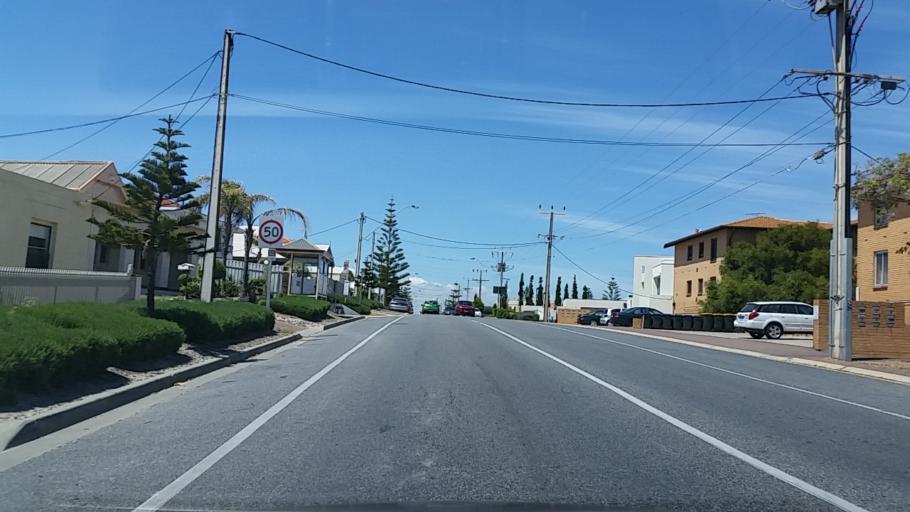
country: AU
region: South Australia
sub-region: Charles Sturt
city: Grange
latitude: -34.9077
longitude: 138.4912
